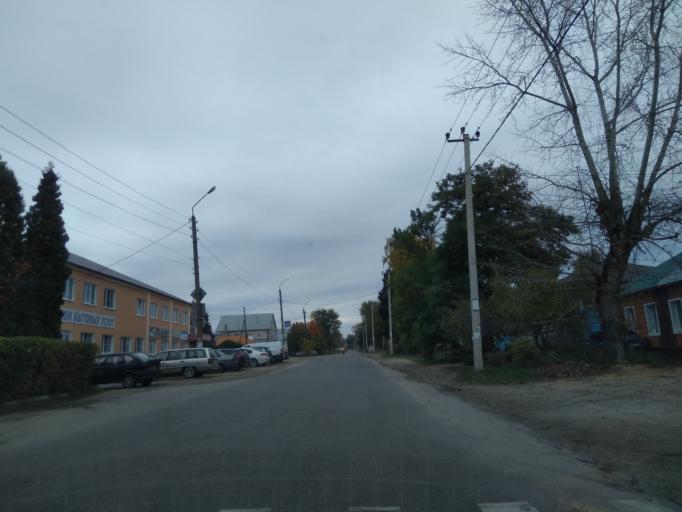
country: RU
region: Lipetsk
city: Zadonsk
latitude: 52.3857
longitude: 38.9195
